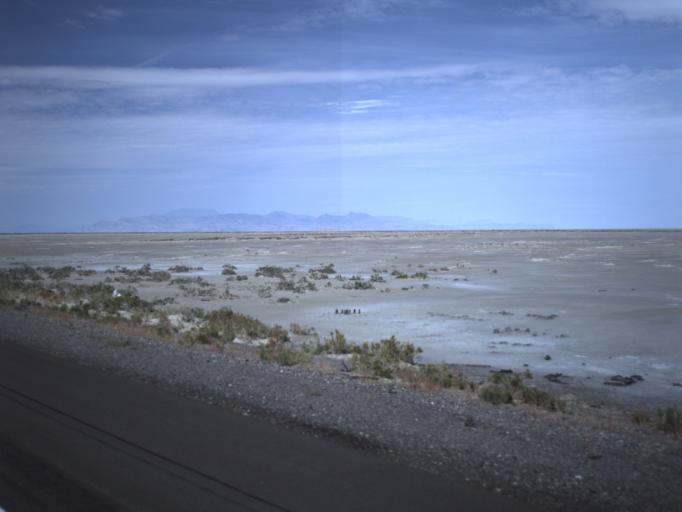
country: US
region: Utah
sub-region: Tooele County
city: Wendover
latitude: 40.7287
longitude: -113.3498
